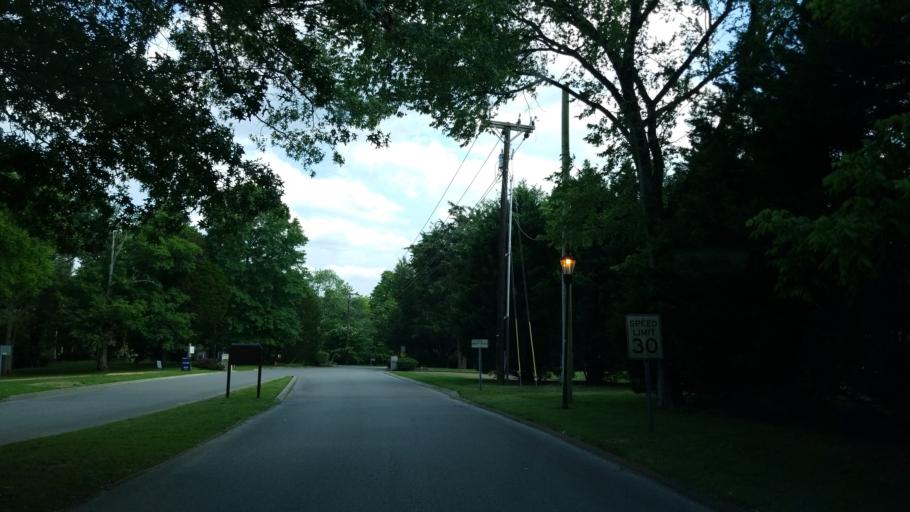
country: US
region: Tennessee
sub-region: Davidson County
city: Forest Hills
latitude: 36.0410
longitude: -86.8250
